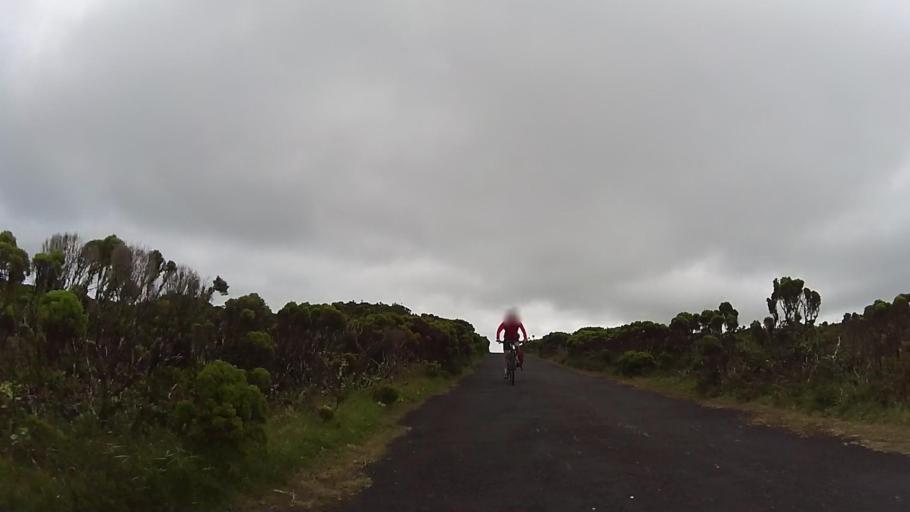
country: PT
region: Azores
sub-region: Sao Roque do Pico
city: Sao Roque do Pico
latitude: 38.4646
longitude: -28.2864
